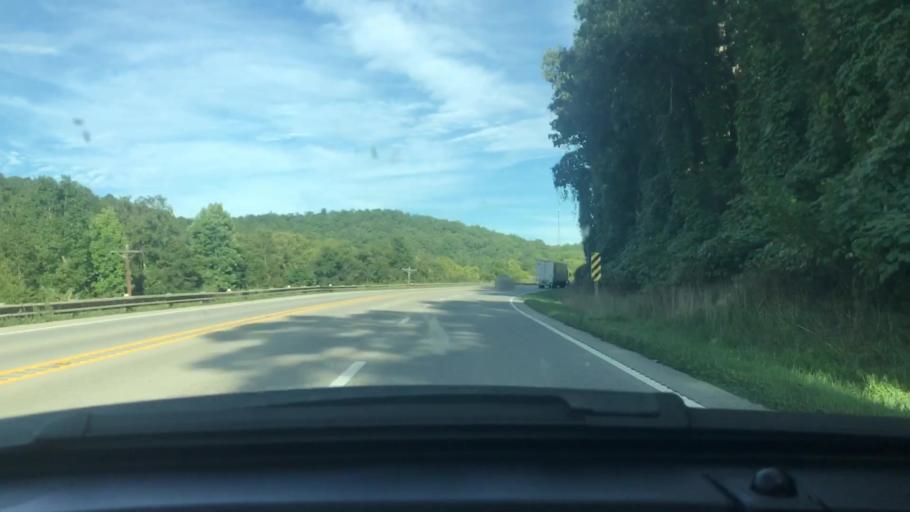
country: US
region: Arkansas
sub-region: Sharp County
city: Cherokee Village
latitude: 36.3039
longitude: -91.4185
